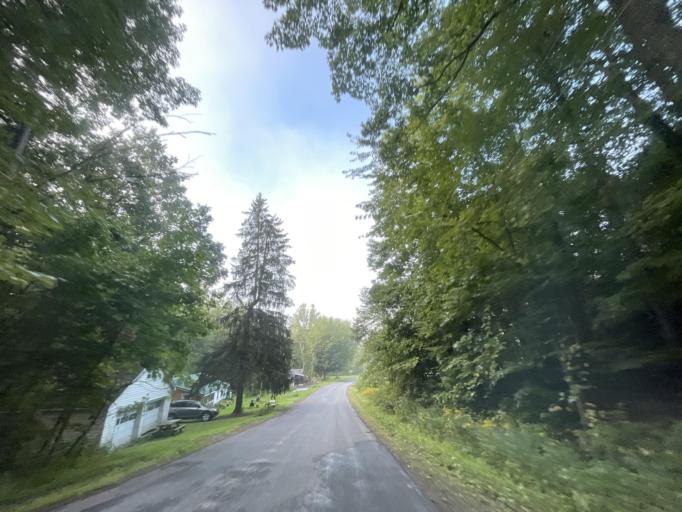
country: US
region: New York
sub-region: Chenango County
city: Oxford
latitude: 42.3914
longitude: -75.6180
